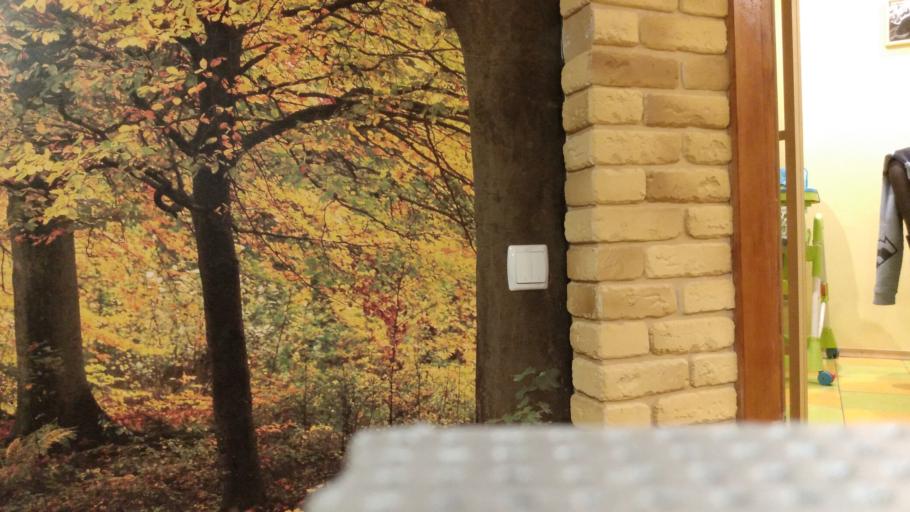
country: RU
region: Vologda
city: Babayevo
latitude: 59.3722
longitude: 35.9937
